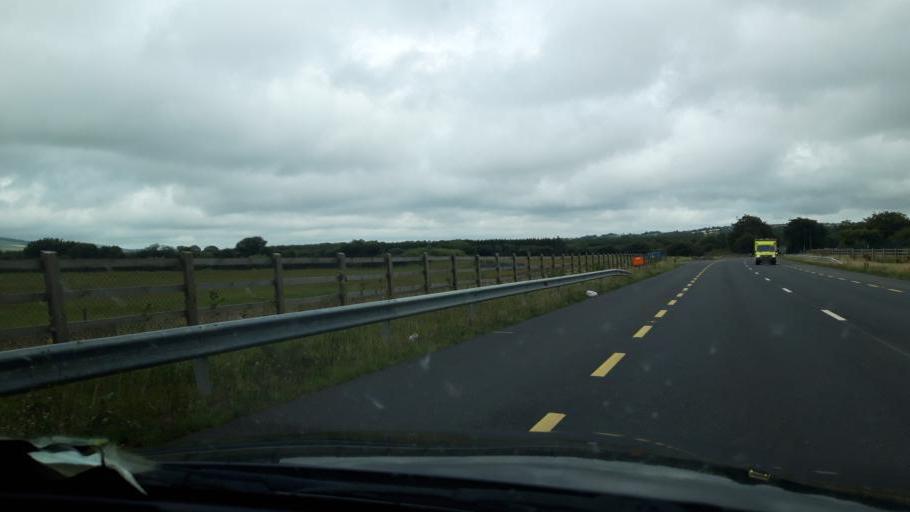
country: IE
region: Leinster
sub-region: Loch Garman
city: New Ross
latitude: 52.4231
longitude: -6.8489
